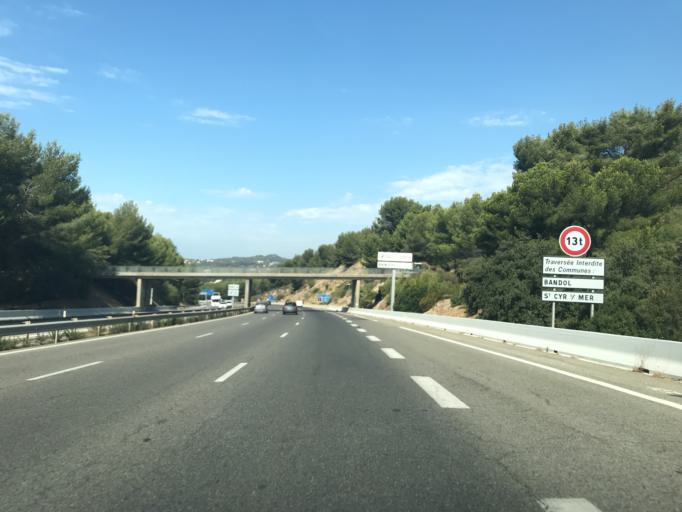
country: FR
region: Provence-Alpes-Cote d'Azur
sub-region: Departement du Var
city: Sanary-sur-Mer
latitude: 43.1456
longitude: 5.7836
